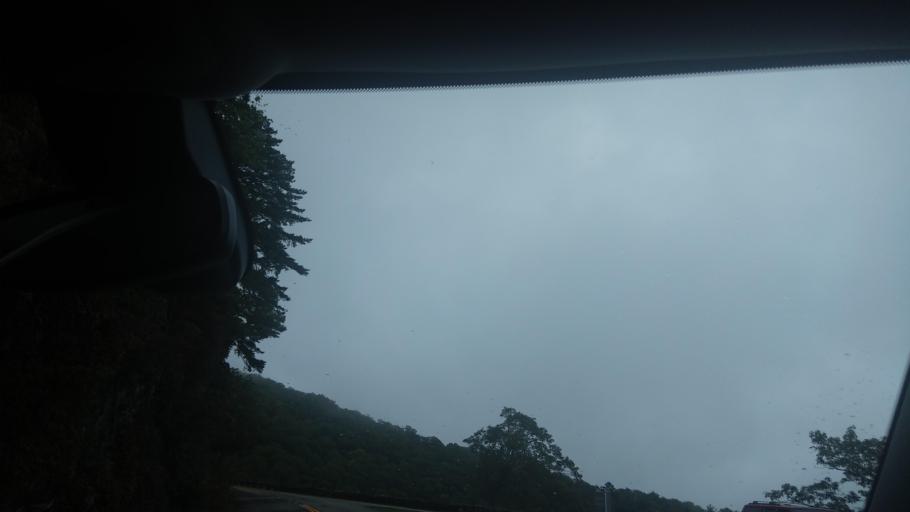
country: US
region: North Carolina
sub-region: Mitchell County
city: Spruce Pine
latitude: 35.9037
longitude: -81.9689
